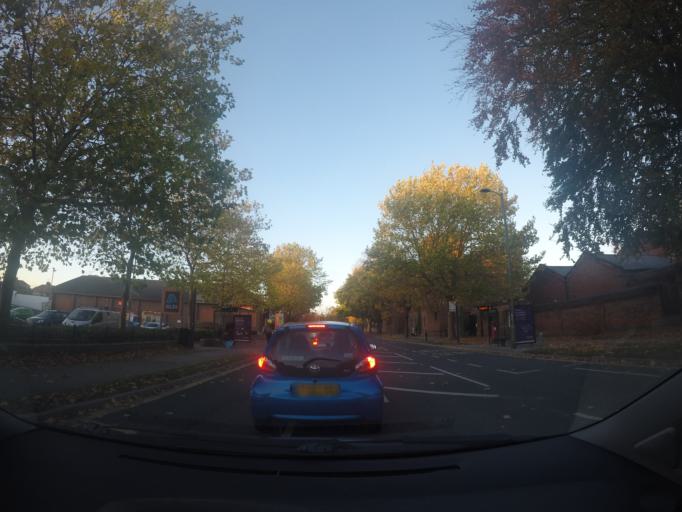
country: GB
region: England
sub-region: City of York
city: Fulford
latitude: 53.9434
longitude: -1.0741
